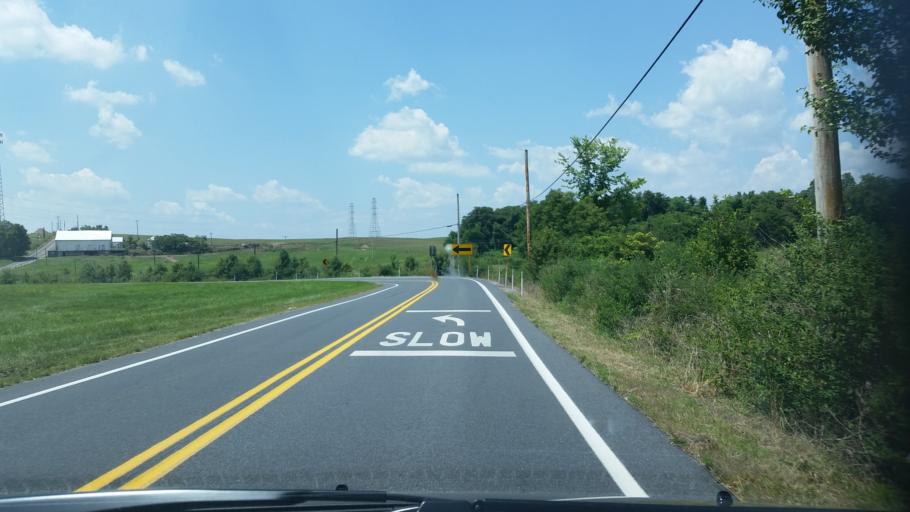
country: US
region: Pennsylvania
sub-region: Dauphin County
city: Hummelstown
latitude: 40.2880
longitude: -76.7284
